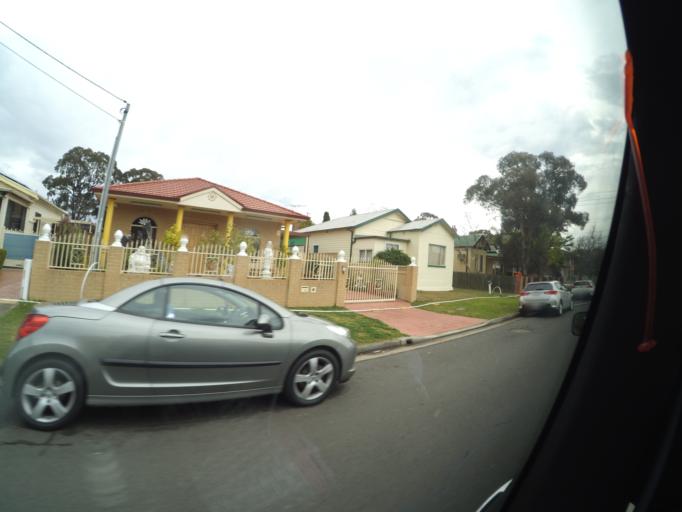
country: AU
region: New South Wales
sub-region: Bankstown
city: Bankstown
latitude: -33.9238
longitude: 151.0251
